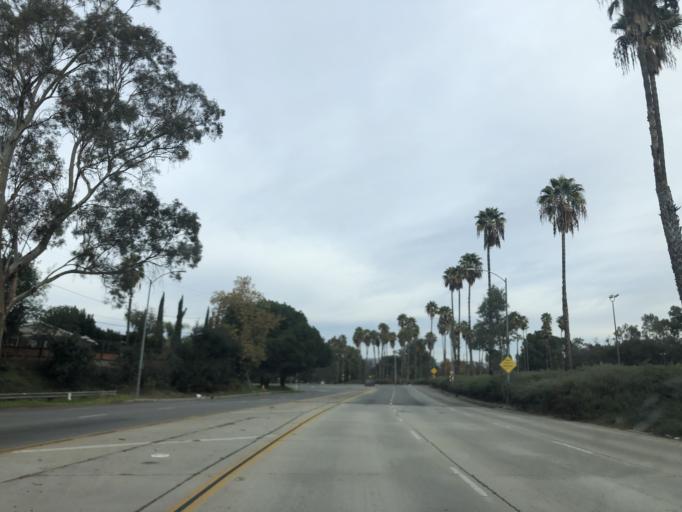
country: US
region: California
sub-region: Los Angeles County
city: Van Nuys
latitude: 34.1703
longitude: -118.4981
